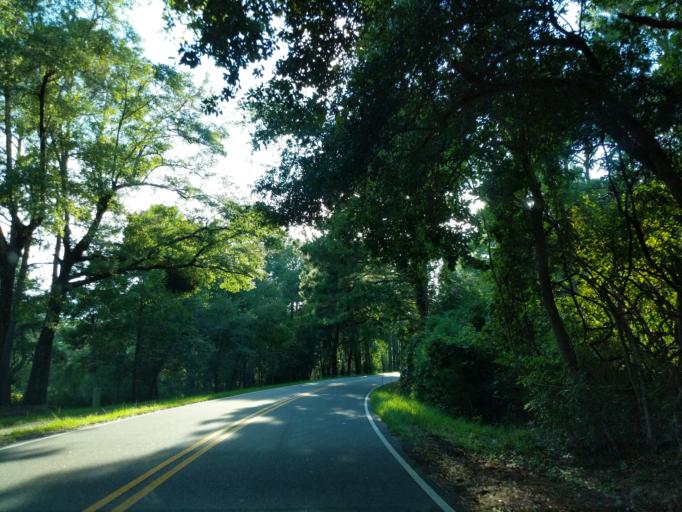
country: US
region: South Carolina
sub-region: Charleston County
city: Awendaw
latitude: 33.0922
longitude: -79.4732
